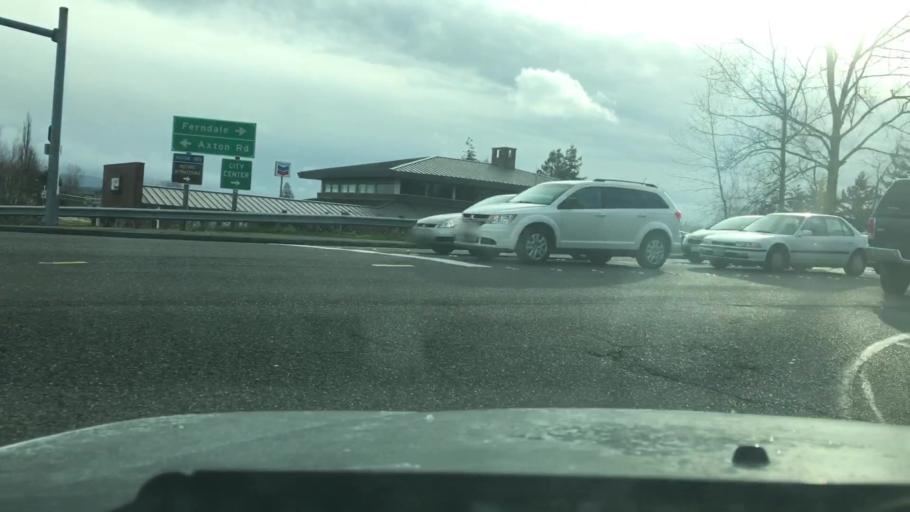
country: US
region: Washington
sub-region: Whatcom County
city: Ferndale
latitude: 48.8476
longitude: -122.5748
